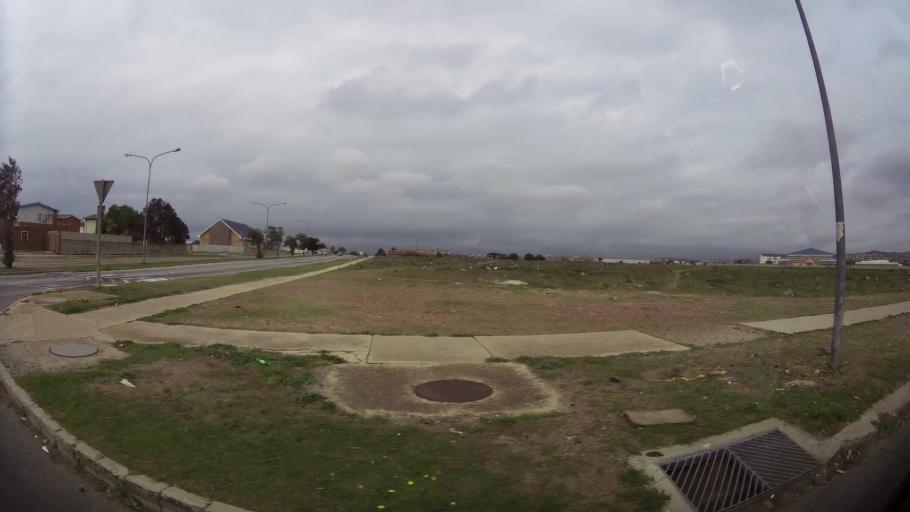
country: ZA
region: Eastern Cape
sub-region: Nelson Mandela Bay Metropolitan Municipality
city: Port Elizabeth
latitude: -33.8952
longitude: 25.5563
